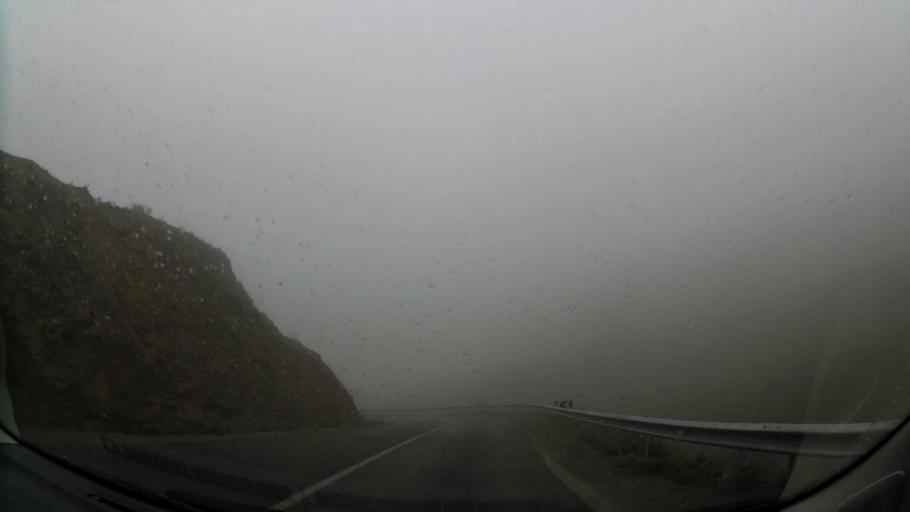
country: MA
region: Oriental
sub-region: Nador
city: Boudinar
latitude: 35.1060
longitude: -3.5623
